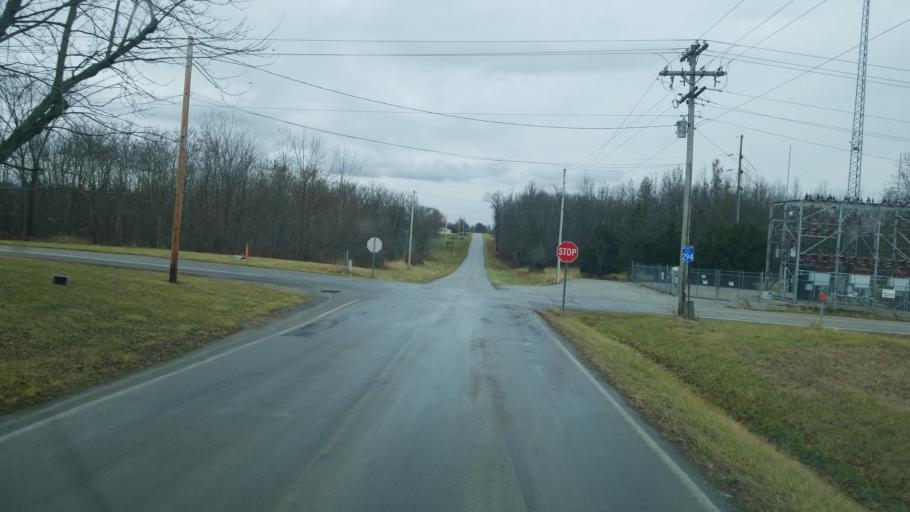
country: US
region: Ohio
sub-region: Hardin County
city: Forest
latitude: 40.7379
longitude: -83.4199
